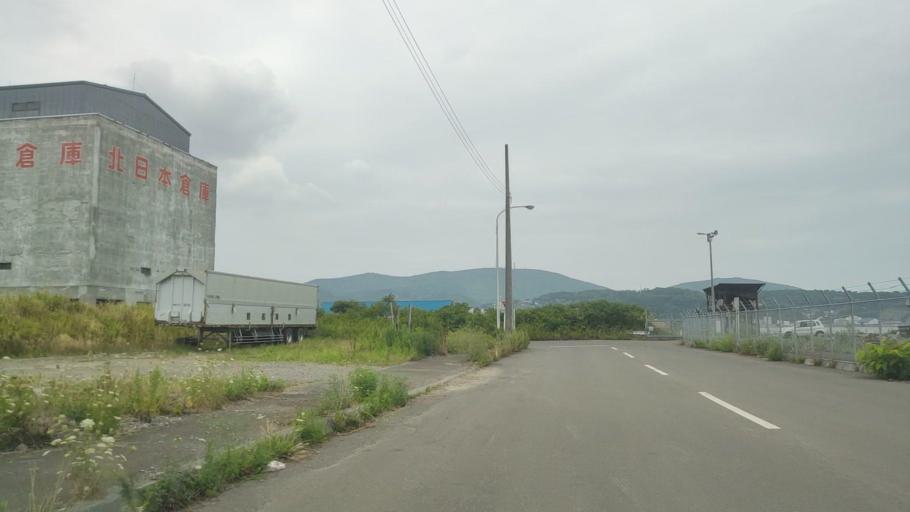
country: JP
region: Hokkaido
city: Otaru
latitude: 43.1983
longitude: 141.0104
